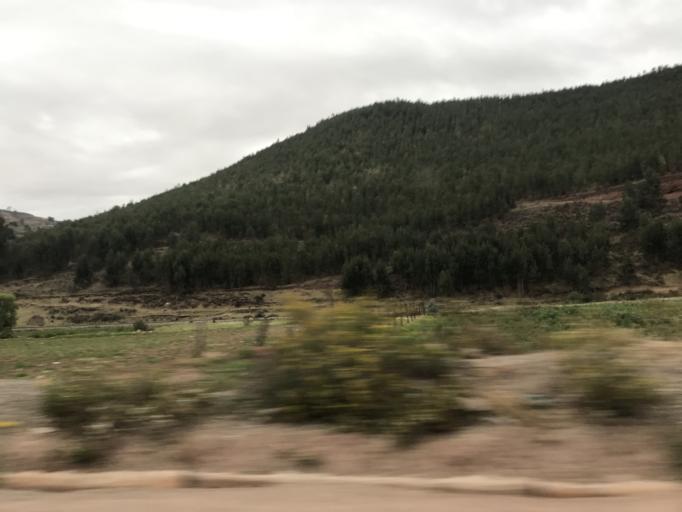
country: PE
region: Cusco
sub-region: Provincia de Anta
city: Huarocondo
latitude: -13.4025
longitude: -72.2096
